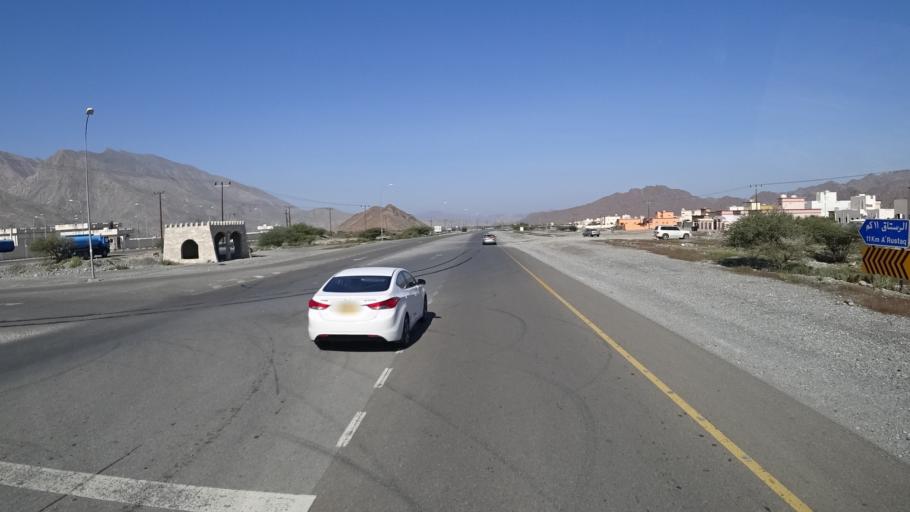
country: OM
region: Al Batinah
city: Bayt al `Awabi
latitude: 23.3420
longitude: 57.4934
